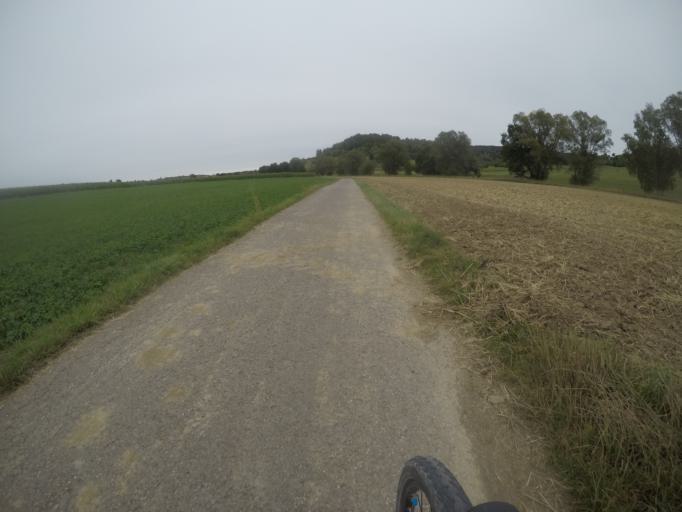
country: DE
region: Baden-Wuerttemberg
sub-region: Karlsruhe Region
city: Heimsheim
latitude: 48.7959
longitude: 8.8498
